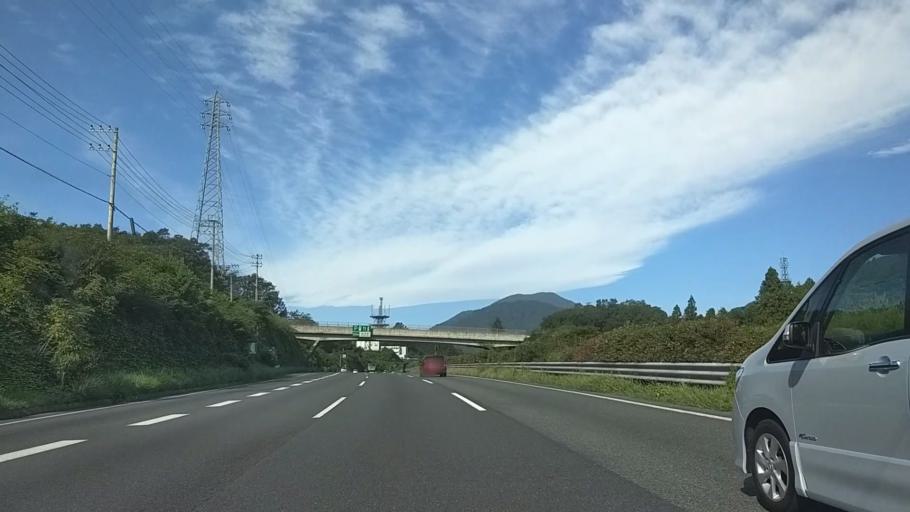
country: JP
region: Yamanashi
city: Uenohara
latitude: 35.6328
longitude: 139.0740
